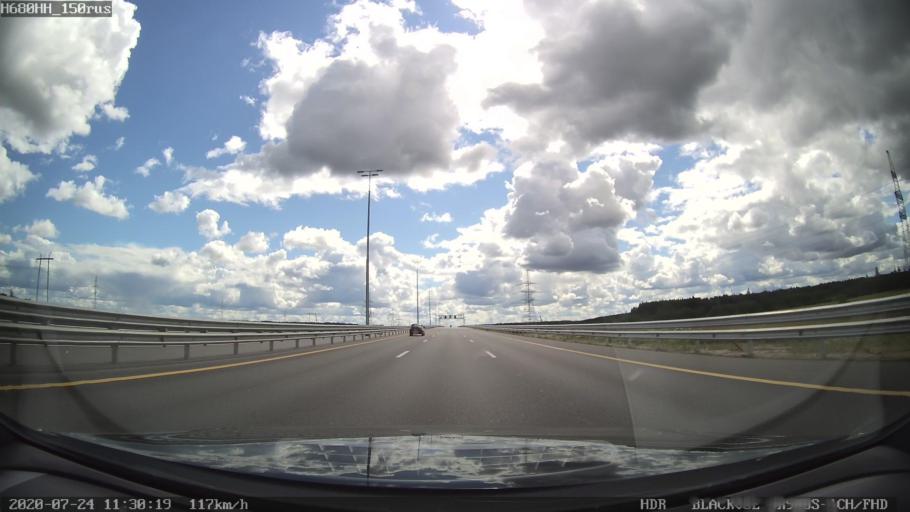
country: RU
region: Leningrad
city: Krasnyy Bor
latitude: 59.6708
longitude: 30.6101
